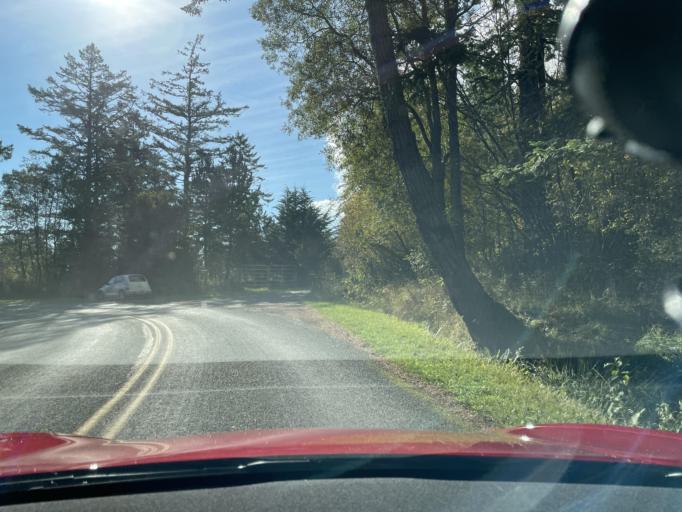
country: US
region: Washington
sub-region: San Juan County
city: Friday Harbor
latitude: 48.5076
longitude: -123.0231
